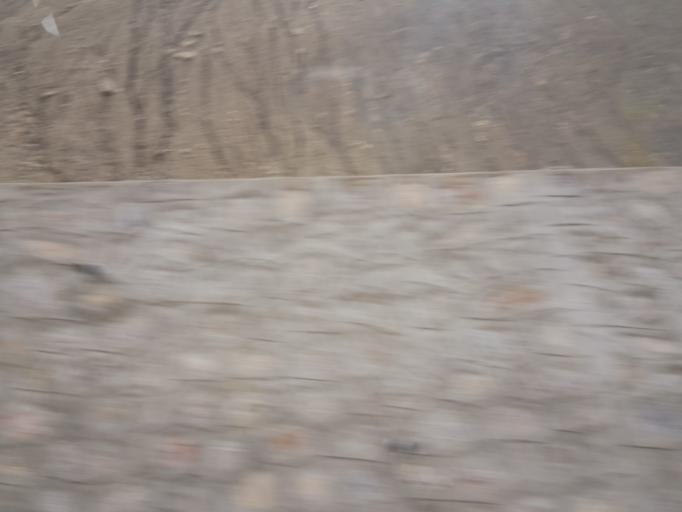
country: TR
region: Sinop
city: Duragan
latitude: 41.4614
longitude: 35.0448
